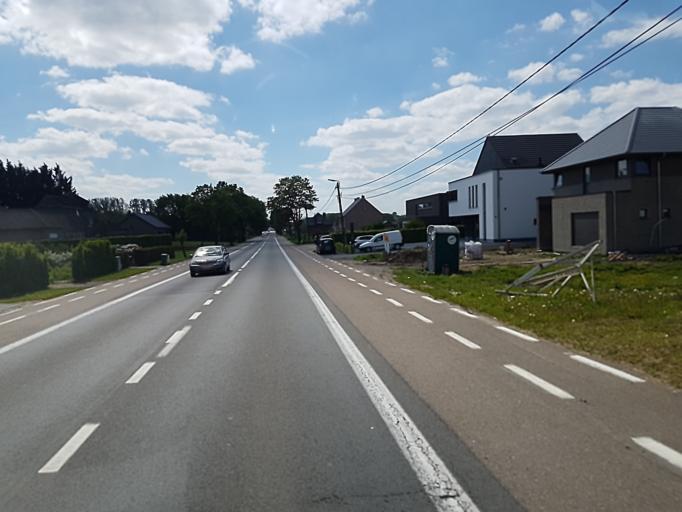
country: BE
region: Flanders
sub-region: Provincie Vlaams-Brabant
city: Glabbeek-Zuurbemde
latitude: 50.8618
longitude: 4.9557
